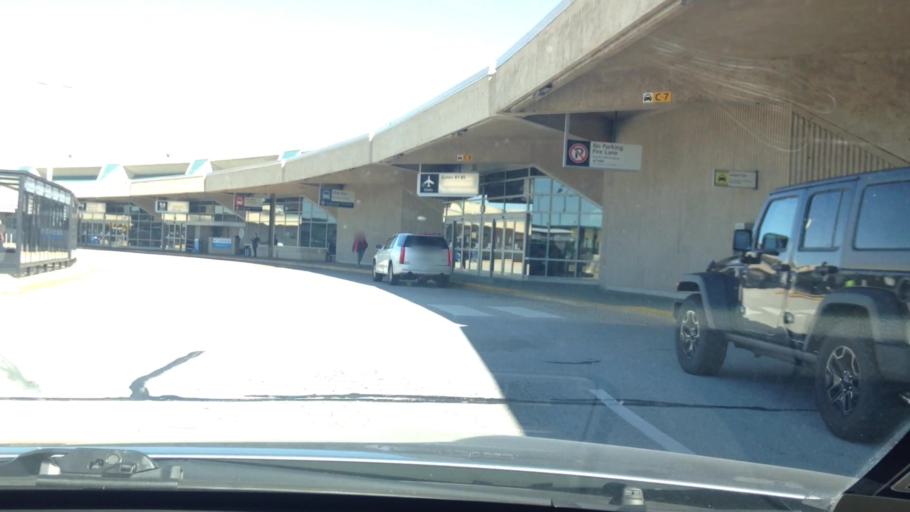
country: US
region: Missouri
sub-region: Platte County
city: Weatherby Lake
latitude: 39.2937
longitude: -94.7121
